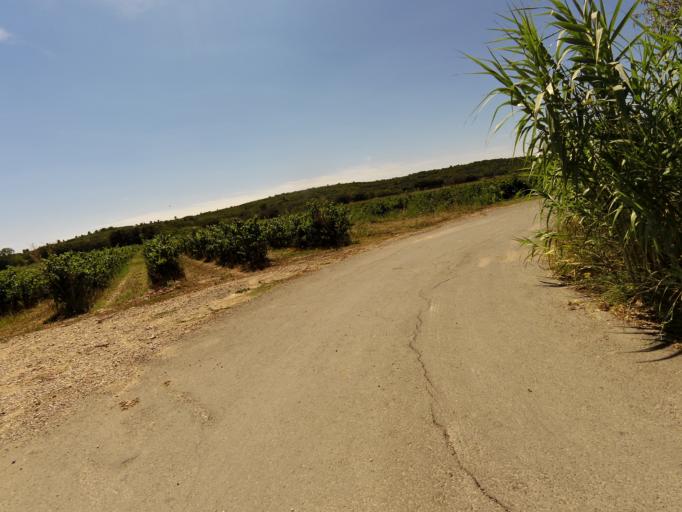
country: FR
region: Languedoc-Roussillon
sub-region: Departement du Gard
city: Aubais
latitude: 43.7544
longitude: 4.1258
